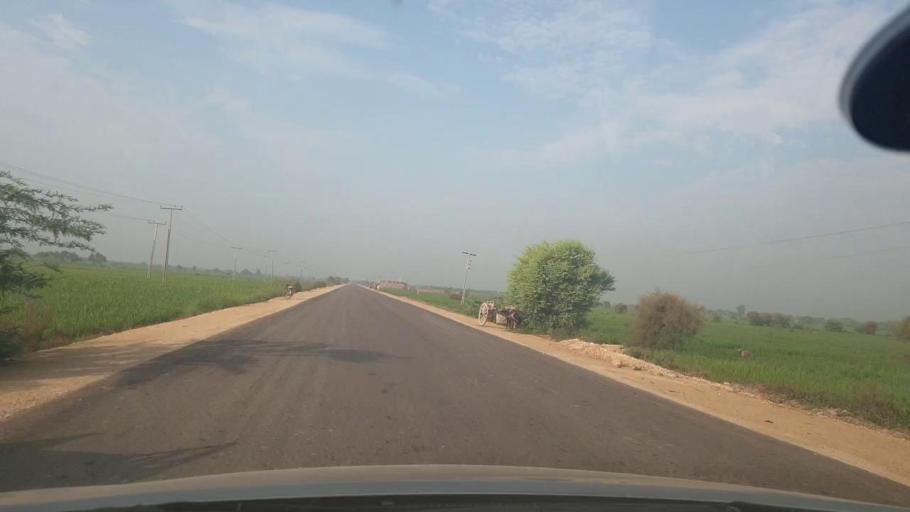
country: PK
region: Sindh
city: Jacobabad
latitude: 28.2572
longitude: 68.4112
